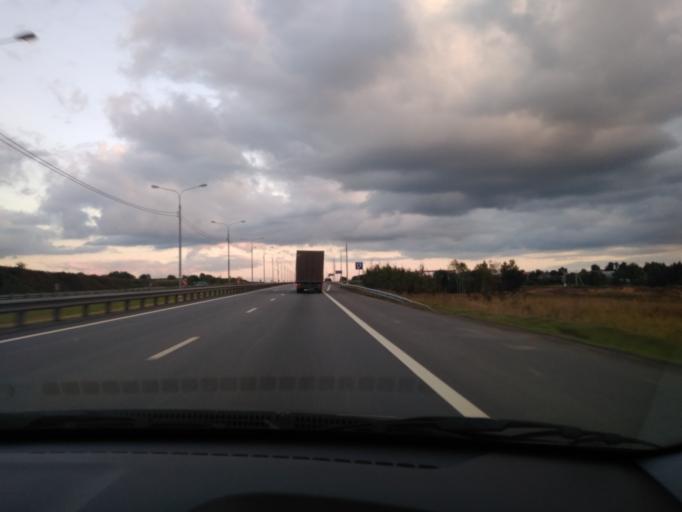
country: RU
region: Moskovskaya
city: Zhukovskiy
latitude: 55.5060
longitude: 38.1396
